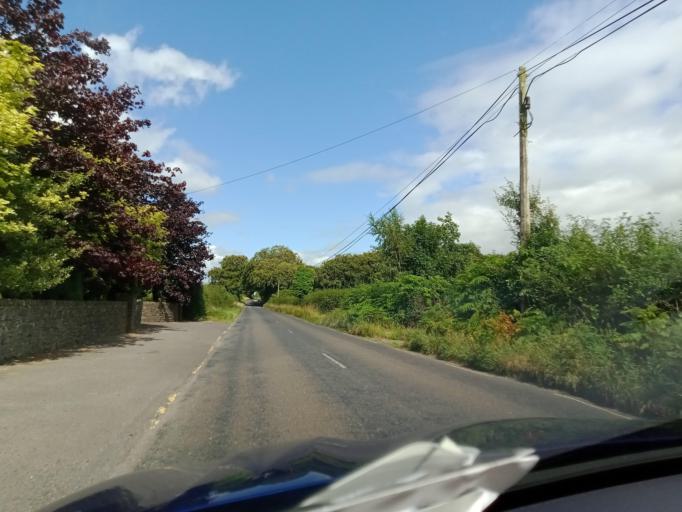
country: IE
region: Leinster
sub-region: Laois
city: Abbeyleix
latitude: 52.9351
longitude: -7.3220
